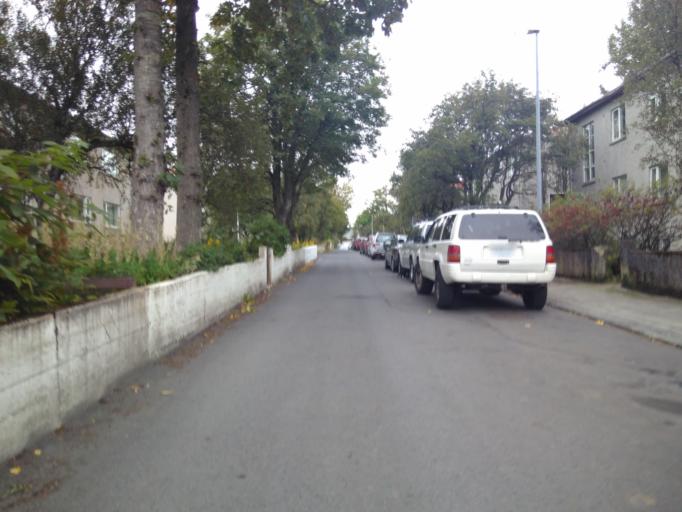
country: IS
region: Capital Region
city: Reykjavik
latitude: 64.1405
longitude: -21.9115
